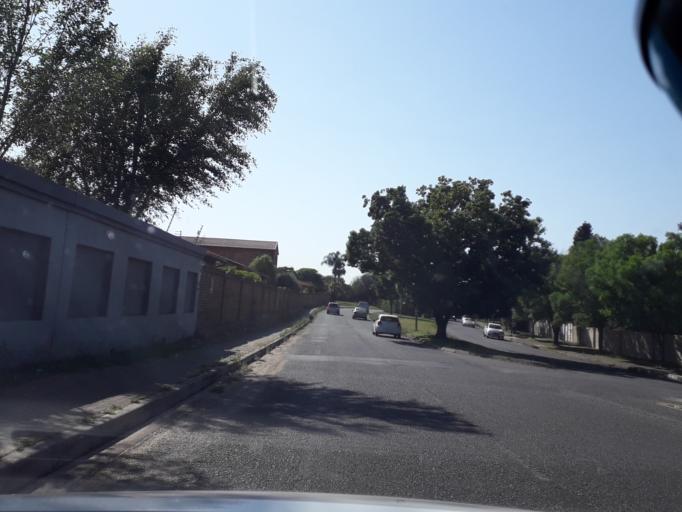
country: ZA
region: Gauteng
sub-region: City of Johannesburg Metropolitan Municipality
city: Roodepoort
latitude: -26.0962
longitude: 27.9476
